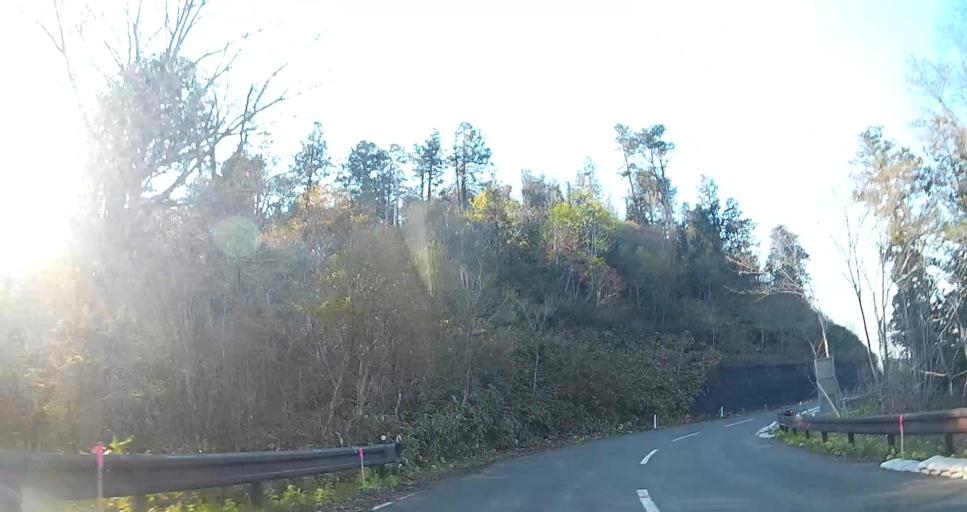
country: JP
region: Aomori
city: Mutsu
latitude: 41.3098
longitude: 141.1128
